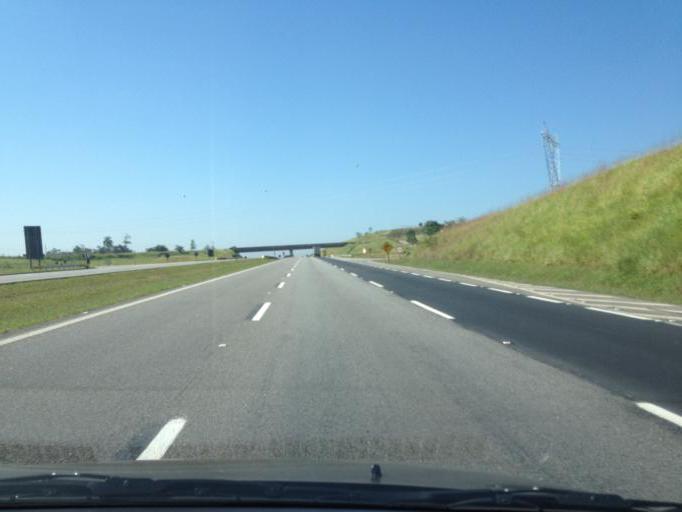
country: BR
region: Sao Paulo
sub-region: Guararema
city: Guararema
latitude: -23.3595
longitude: -46.1041
